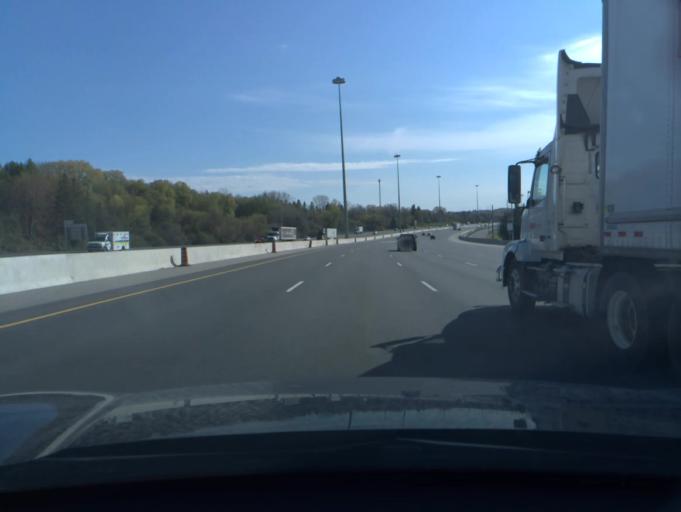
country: CA
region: Ontario
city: North Perth
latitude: 43.8222
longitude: -81.0001
